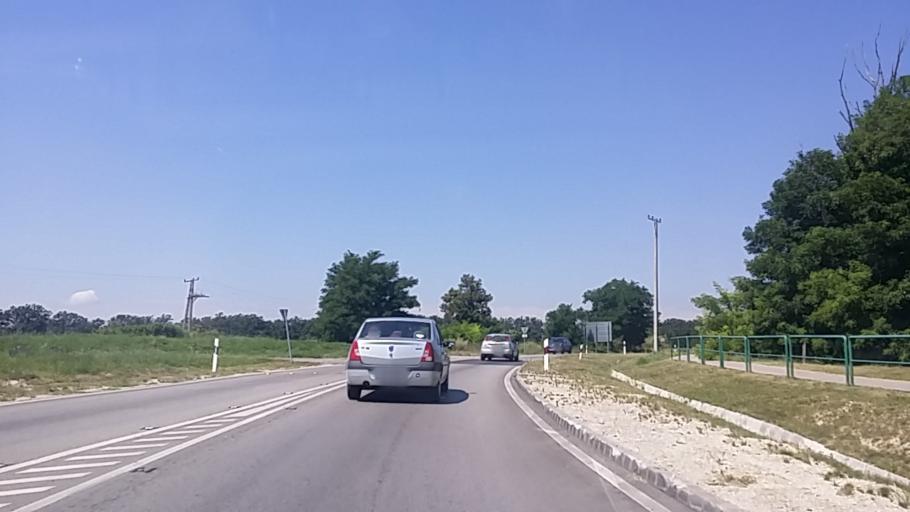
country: HU
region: Zala
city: Keszthely
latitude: 46.7781
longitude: 17.2261
